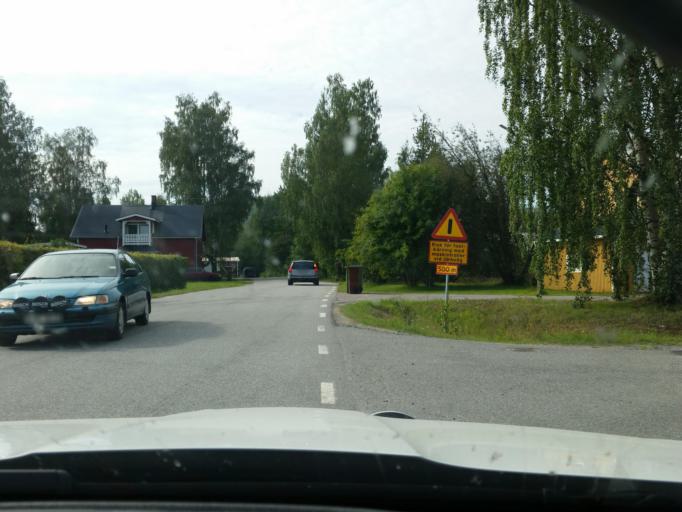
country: SE
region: Norrbotten
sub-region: Alvsbyns Kommun
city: AElvsbyn
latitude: 65.6686
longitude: 20.8701
